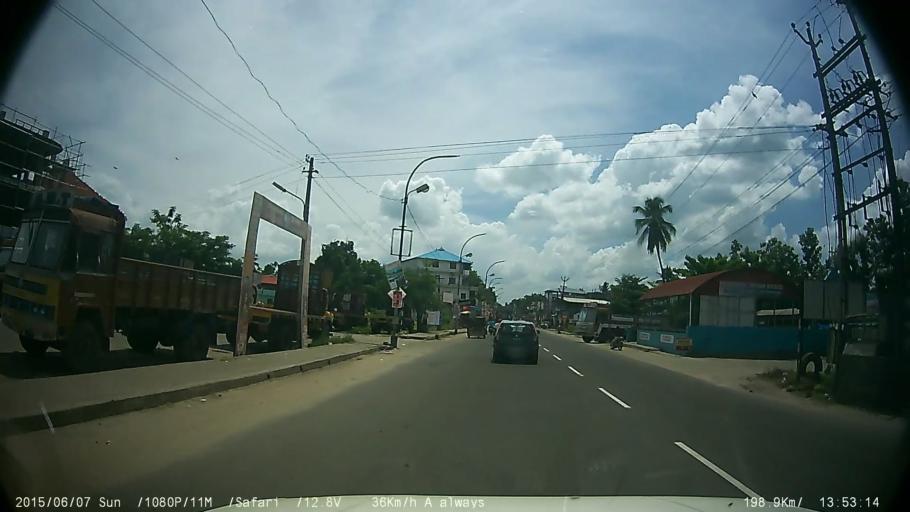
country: IN
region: Kerala
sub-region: Ernakulam
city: Angamali
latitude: 10.1673
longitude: 76.4362
